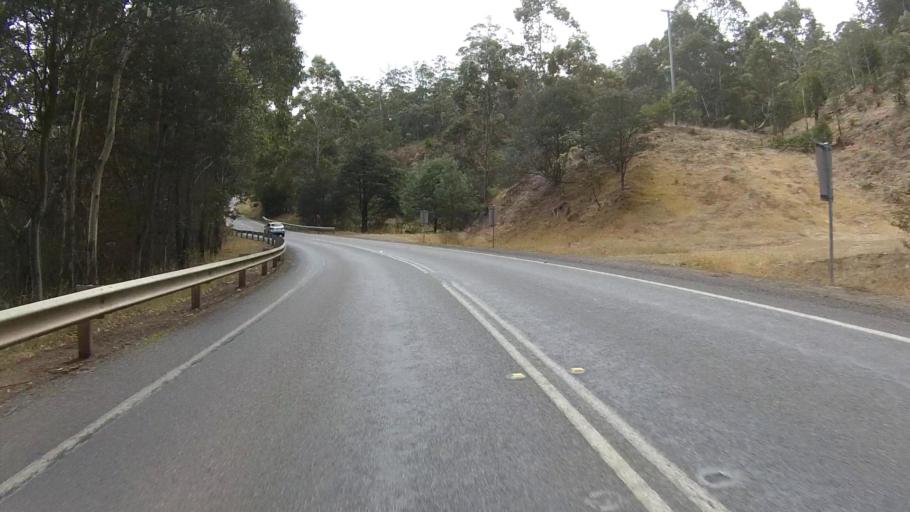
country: AU
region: Tasmania
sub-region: Kingborough
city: Kettering
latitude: -43.1020
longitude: 147.2449
